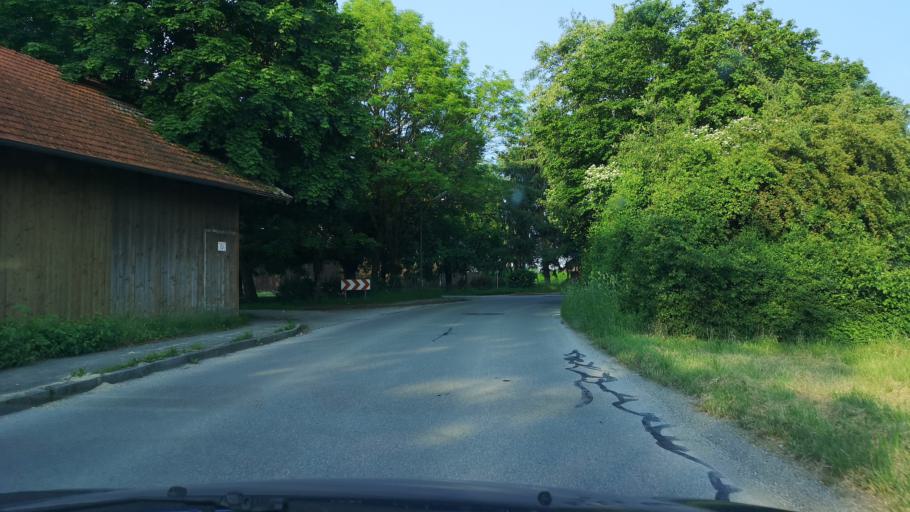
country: DE
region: Bavaria
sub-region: Upper Bavaria
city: Kirchheim bei Muenchen
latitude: 48.1715
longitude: 11.7770
